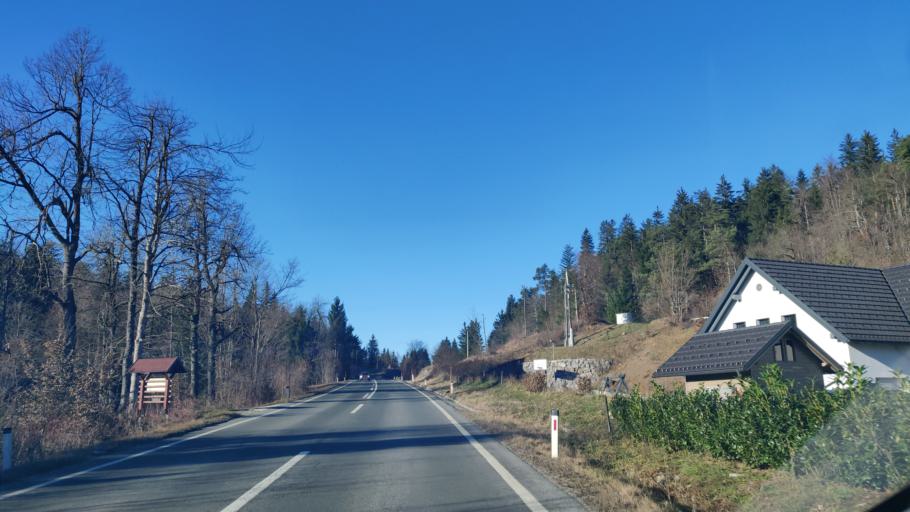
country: SI
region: Logatec
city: Logatec
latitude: 45.8802
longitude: 14.2068
